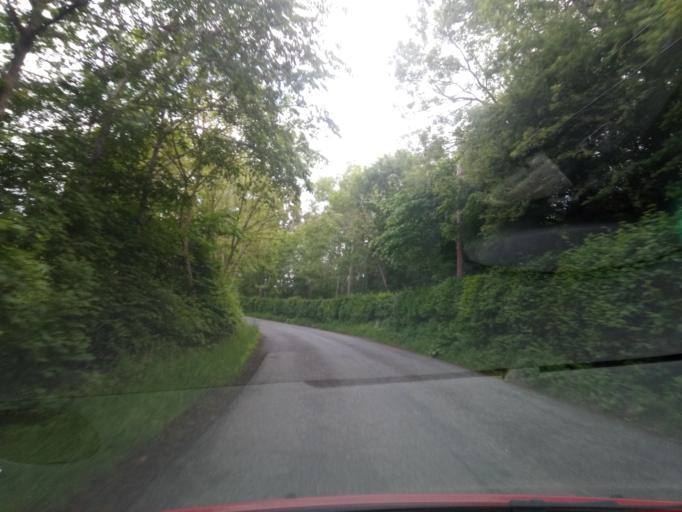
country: GB
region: Scotland
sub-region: The Scottish Borders
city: Selkirk
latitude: 55.5380
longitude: -2.8620
